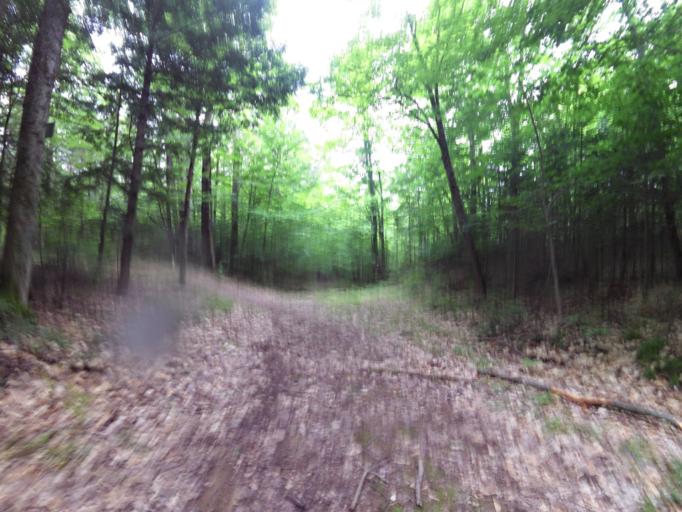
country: CA
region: Quebec
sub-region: Outaouais
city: Wakefield
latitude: 45.6146
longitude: -76.0466
